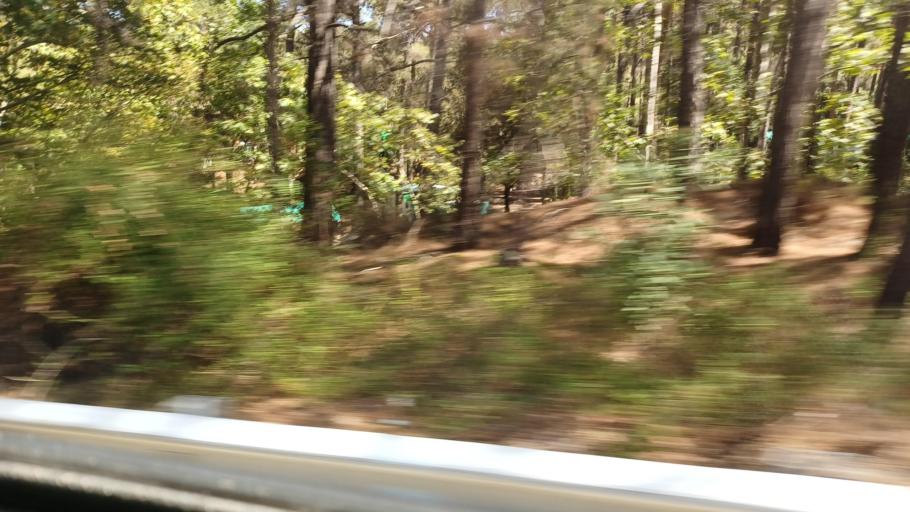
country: CY
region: Lefkosia
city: Kakopetria
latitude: 34.9515
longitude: 32.9257
